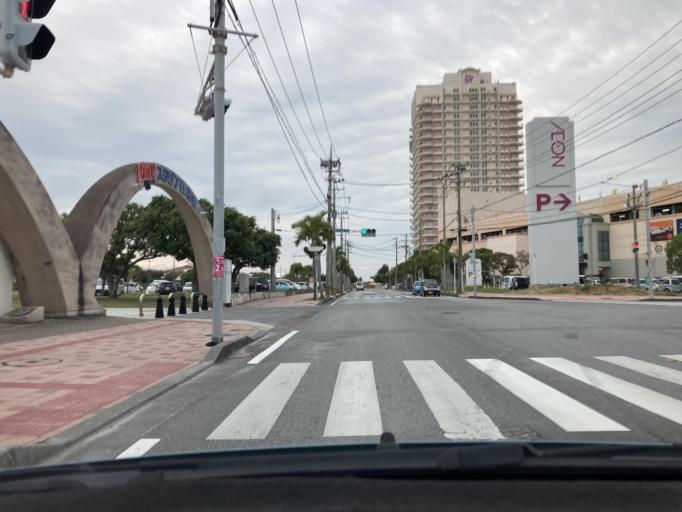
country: JP
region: Okinawa
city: Chatan
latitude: 26.3134
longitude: 127.7585
